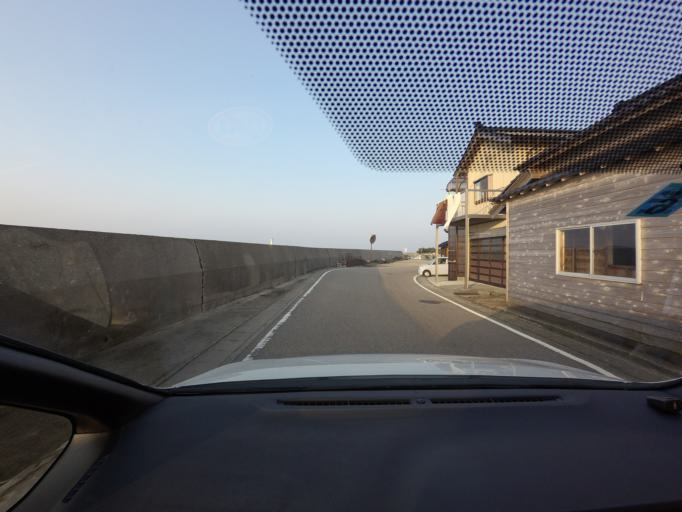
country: JP
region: Ishikawa
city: Nanao
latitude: 37.1667
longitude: 137.0335
